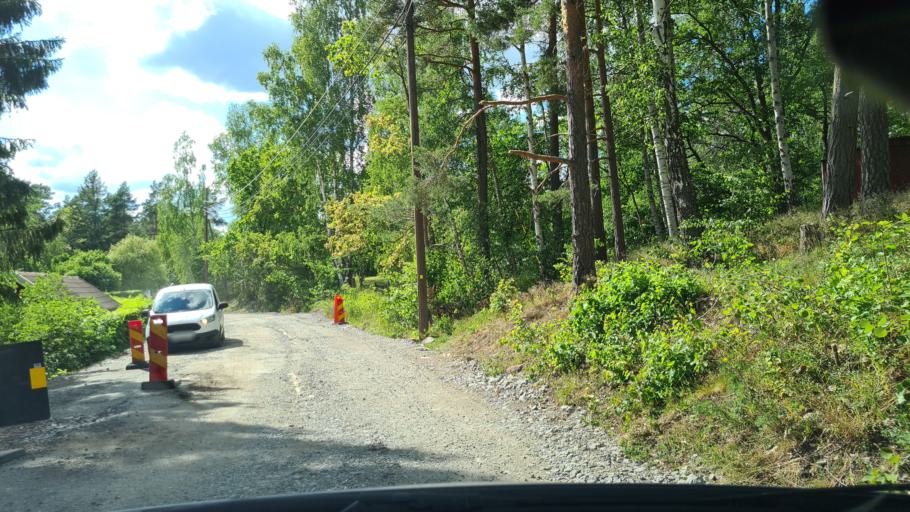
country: SE
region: Stockholm
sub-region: Vaxholms Kommun
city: Vaxholm
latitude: 59.4101
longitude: 18.3818
